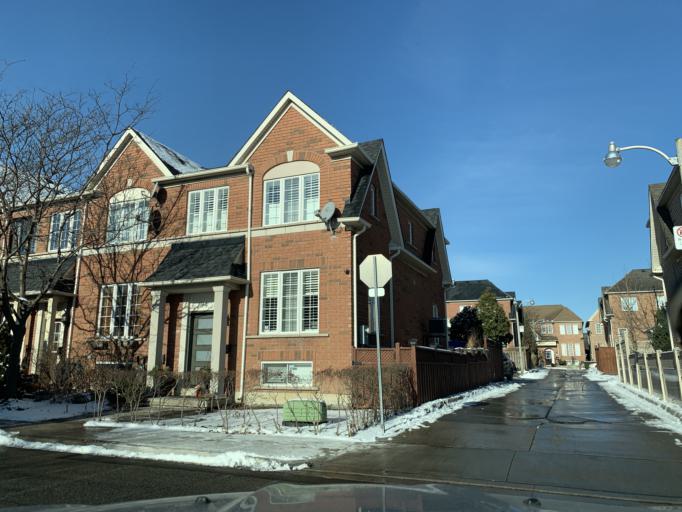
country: CA
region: Ontario
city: Toronto
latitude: 43.6715
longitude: -79.4754
